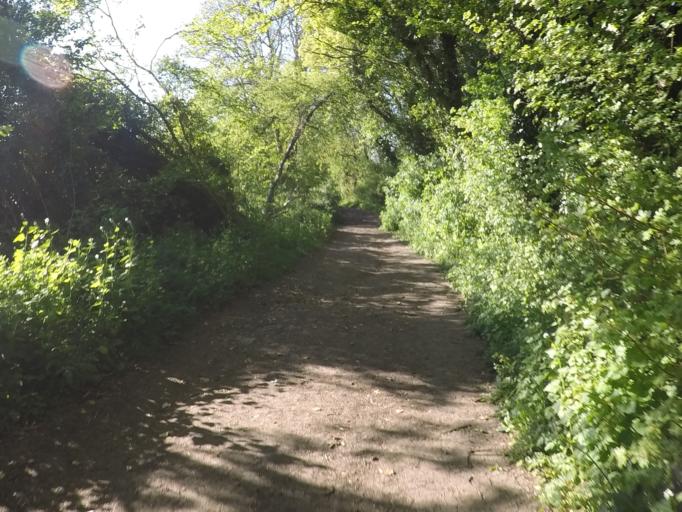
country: GB
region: England
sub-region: Oxfordshire
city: Charlbury
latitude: 51.8742
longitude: -1.4650
